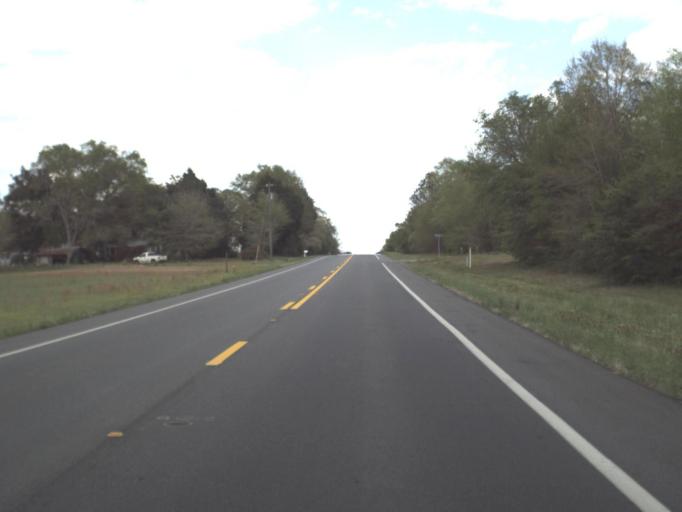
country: US
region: Florida
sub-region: Okaloosa County
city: Crestview
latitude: 30.8731
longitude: -86.5195
